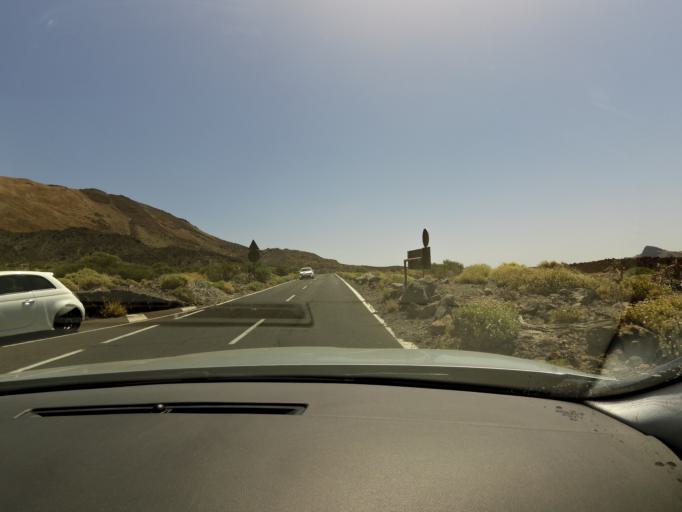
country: ES
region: Canary Islands
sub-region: Provincia de Santa Cruz de Tenerife
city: Vilaflor
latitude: 28.2548
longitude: -16.6212
